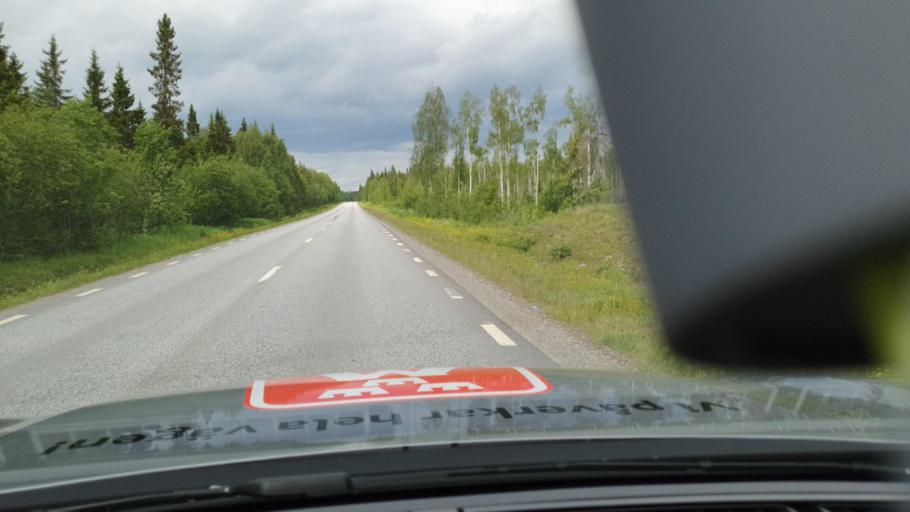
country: SE
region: Norrbotten
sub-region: Lulea Kommun
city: Lulea
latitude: 65.6742
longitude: 22.2219
